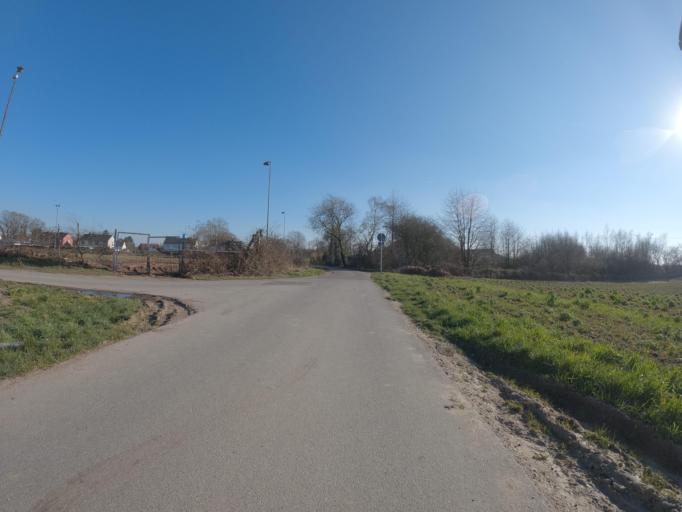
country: DE
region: North Rhine-Westphalia
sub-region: Regierungsbezirk Koln
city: Alsdorf
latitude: 50.8591
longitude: 6.1812
